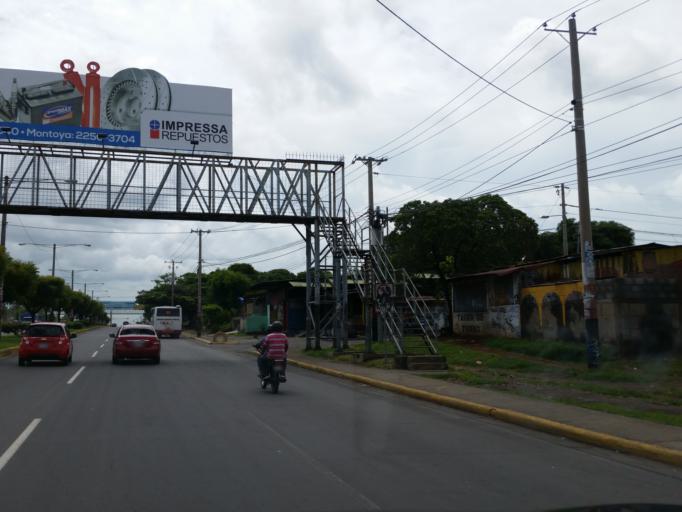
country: NI
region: Managua
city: Managua
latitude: 12.1476
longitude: -86.1905
